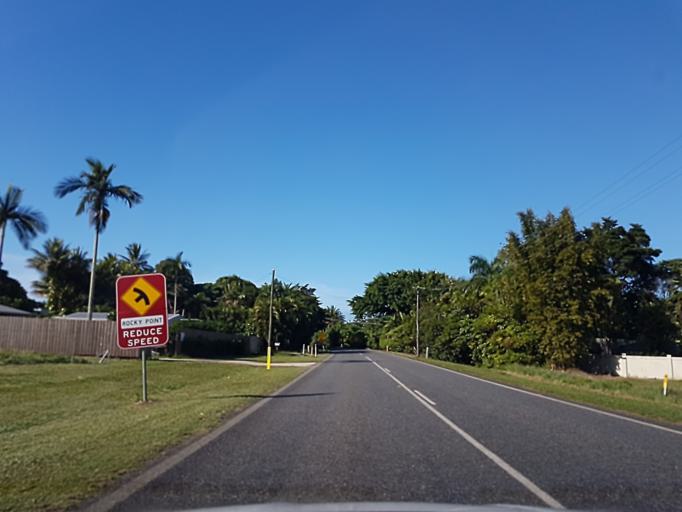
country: AU
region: Queensland
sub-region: Cairns
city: Port Douglas
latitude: -16.3904
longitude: 145.4160
